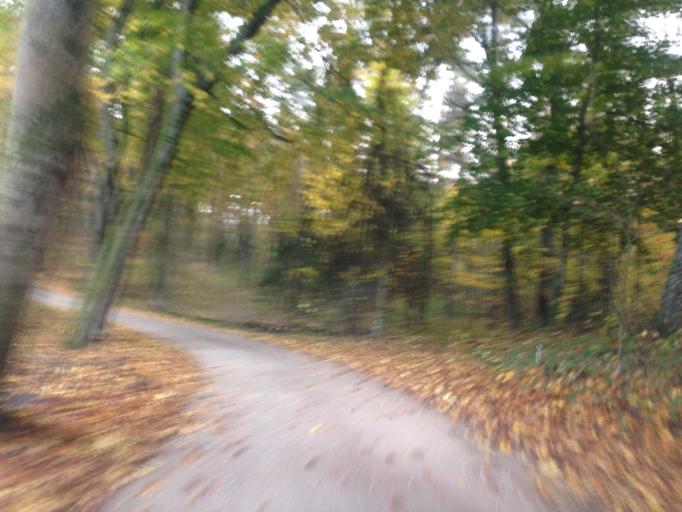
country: PL
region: Kujawsko-Pomorskie
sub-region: Powiat brodnicki
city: Gorzno
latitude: 53.2420
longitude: 19.6797
